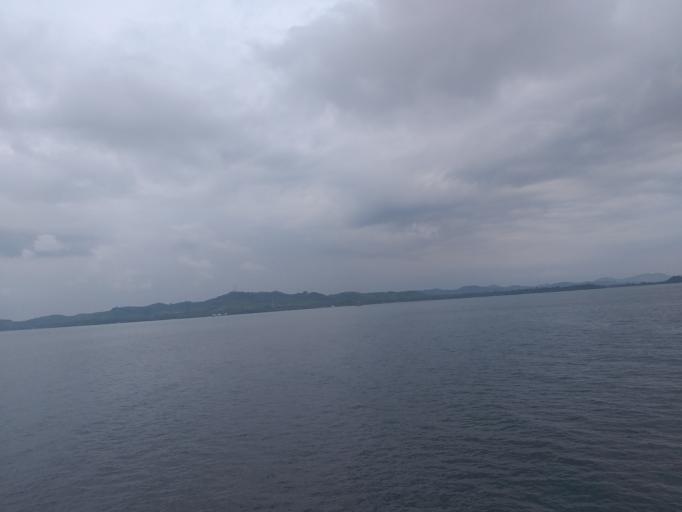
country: TH
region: Trat
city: Laem Ngop
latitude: 12.1596
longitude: 102.2909
